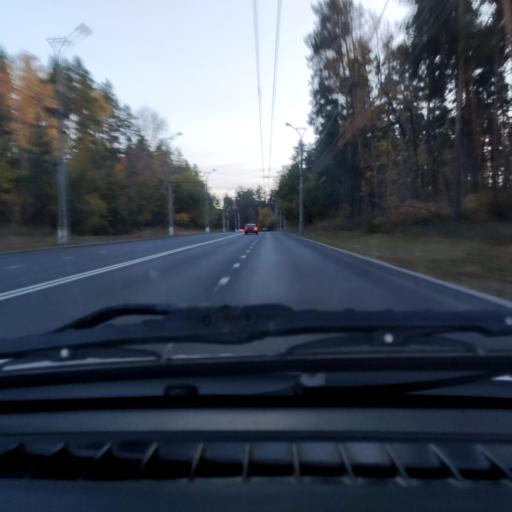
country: RU
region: Samara
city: Zhigulevsk
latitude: 53.4902
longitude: 49.4627
